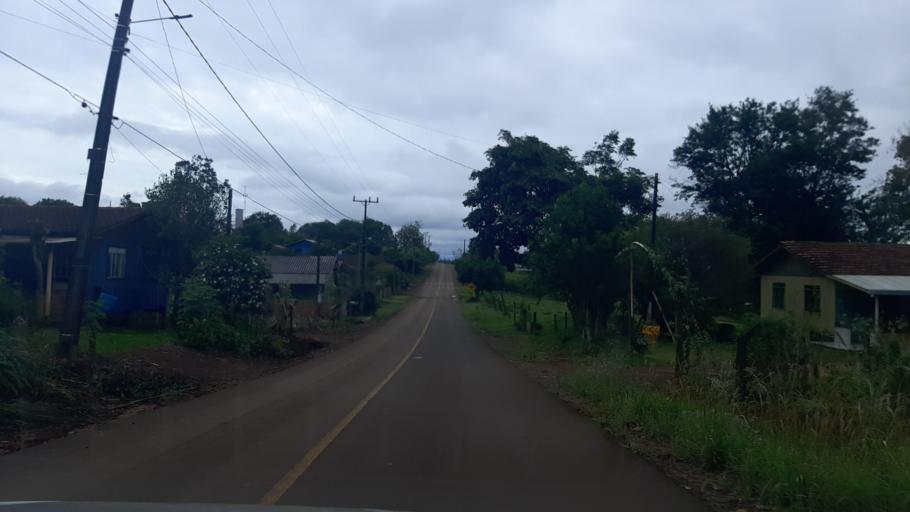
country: BR
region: Parana
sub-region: Ampere
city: Ampere
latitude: -26.0368
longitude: -53.5078
